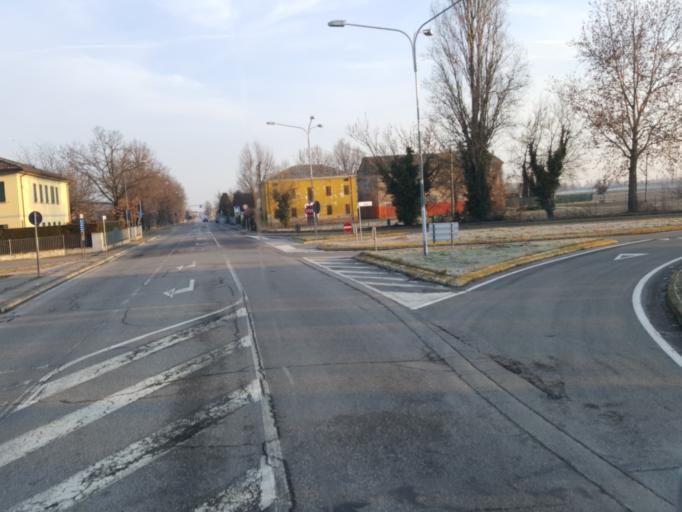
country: IT
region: Emilia-Romagna
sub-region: Provincia di Parma
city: Sorbolo
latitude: 44.8537
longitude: 10.4517
